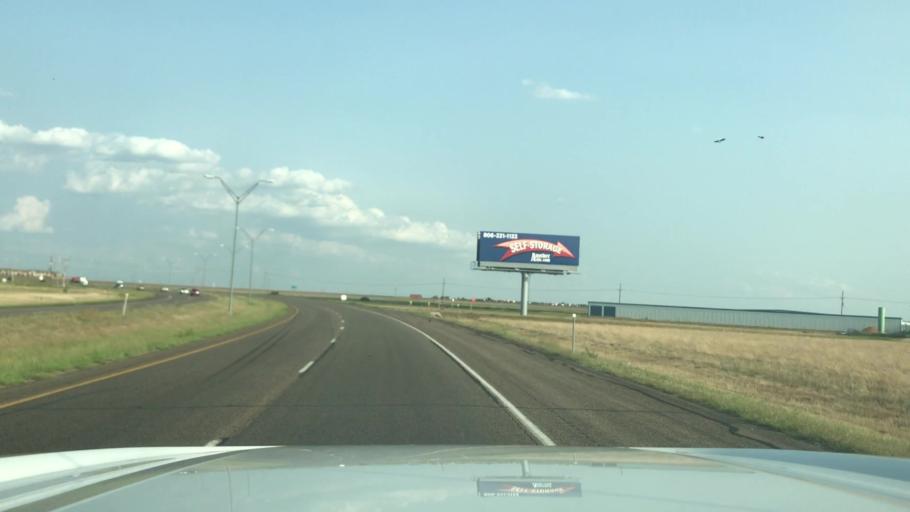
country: US
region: Texas
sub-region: Randall County
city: Canyon
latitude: 35.1197
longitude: -101.9365
